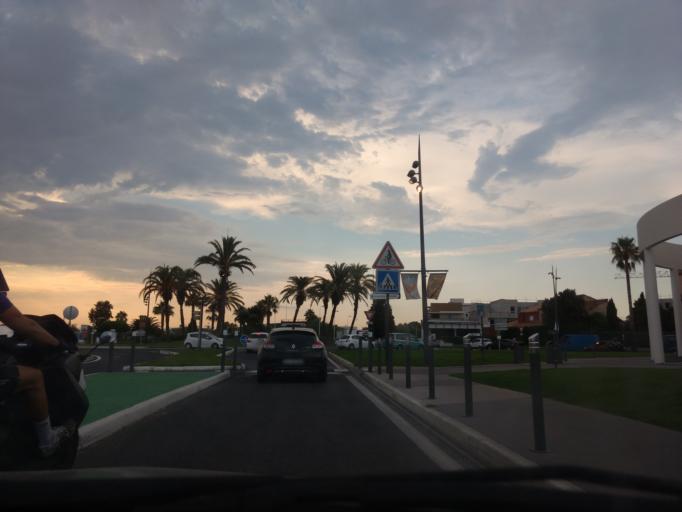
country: FR
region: Languedoc-Roussillon
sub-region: Departement des Pyrenees-Orientales
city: Canet-en-Roussillon
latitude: 42.6978
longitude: 3.0237
